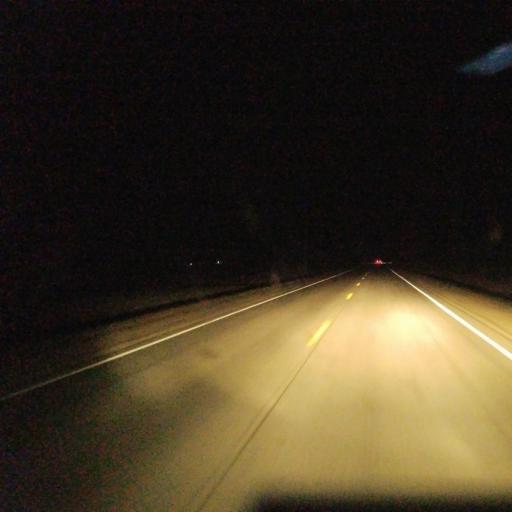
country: US
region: Illinois
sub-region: Knox County
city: Abingdon
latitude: 40.7297
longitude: -90.4693
